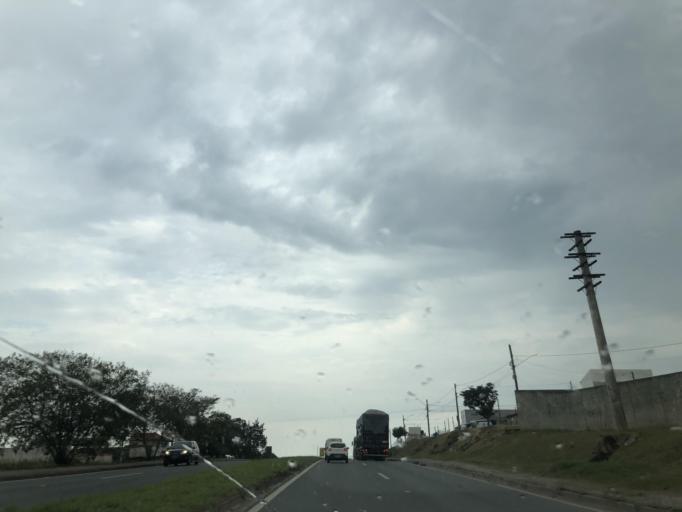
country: BR
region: Sao Paulo
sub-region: Salto De Pirapora
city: Salto de Pirapora
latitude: -23.6413
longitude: -47.5792
